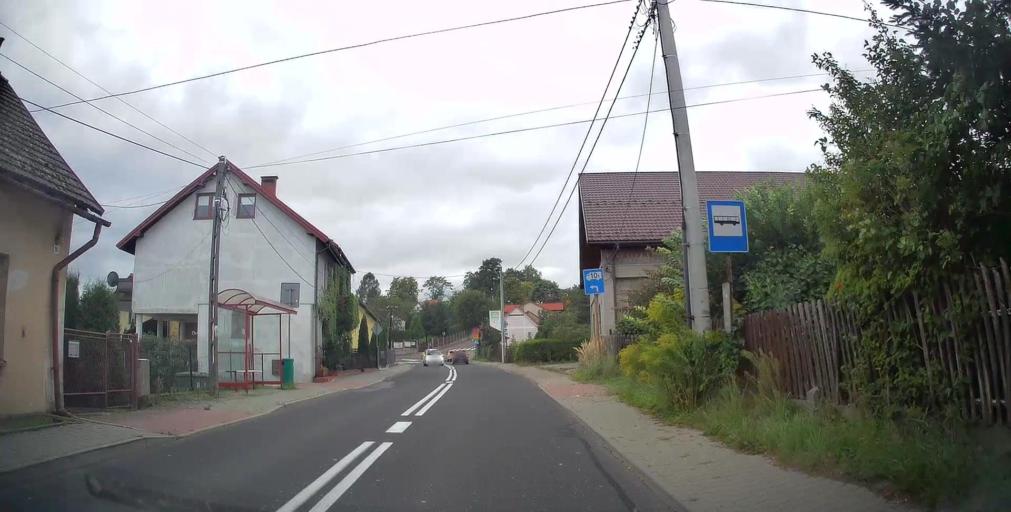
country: PL
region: Lesser Poland Voivodeship
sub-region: Powiat chrzanowski
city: Alwernia
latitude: 50.0698
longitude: 19.5426
